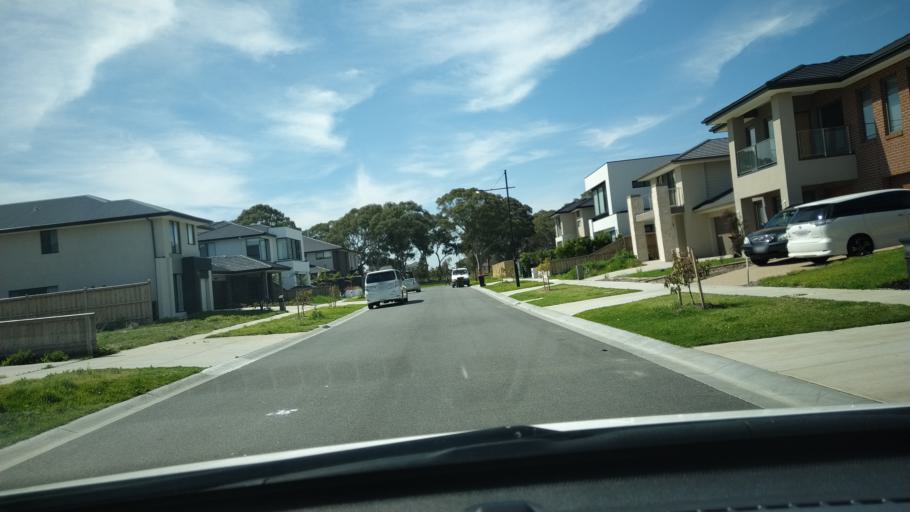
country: AU
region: Victoria
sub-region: Greater Dandenong
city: Keysborough
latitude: -38.0035
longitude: 145.1750
